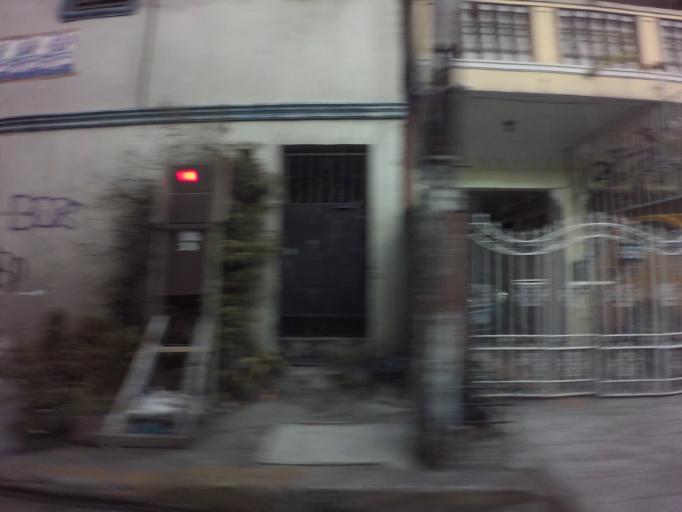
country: PH
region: Metro Manila
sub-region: Makati City
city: Makati City
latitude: 14.5630
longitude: 121.0495
